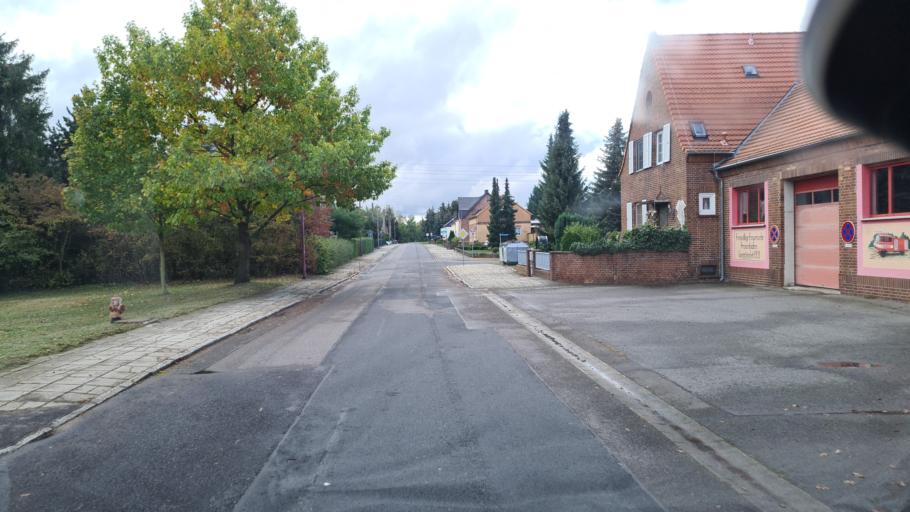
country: DE
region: Brandenburg
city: Grossraschen
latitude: 51.5817
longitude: 13.9615
